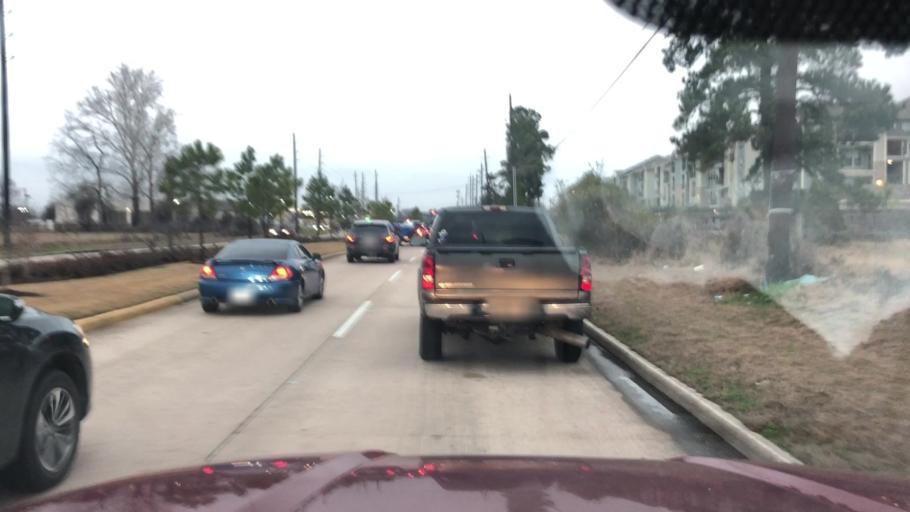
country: US
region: Texas
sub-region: Harris County
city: Tomball
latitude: 30.0432
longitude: -95.5380
